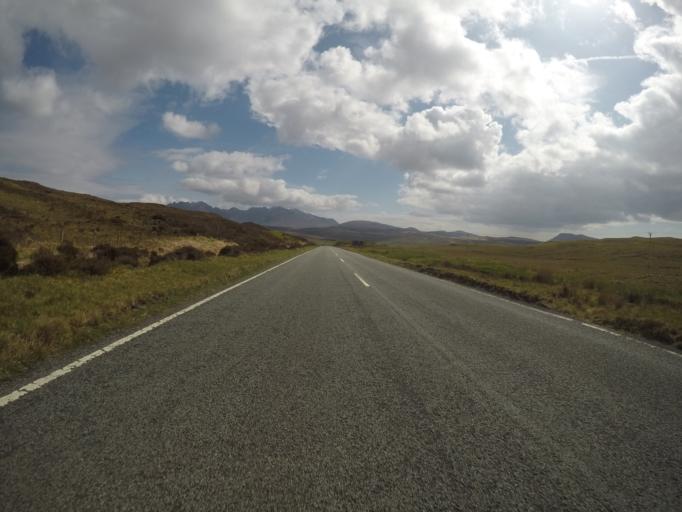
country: GB
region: Scotland
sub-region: Highland
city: Isle of Skye
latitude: 57.3106
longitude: -6.3184
